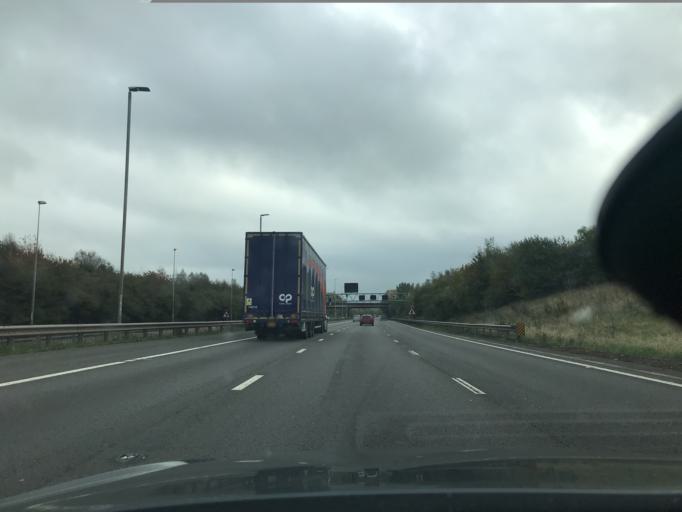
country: GB
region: England
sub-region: Solihull
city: Chelmsley Wood
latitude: 52.4979
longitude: -1.7175
